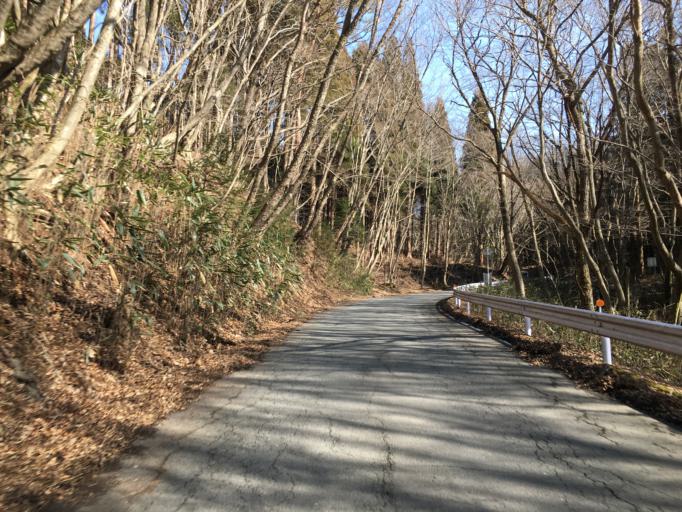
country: JP
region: Ibaraki
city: Kitaibaraki
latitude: 36.8324
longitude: 140.5587
